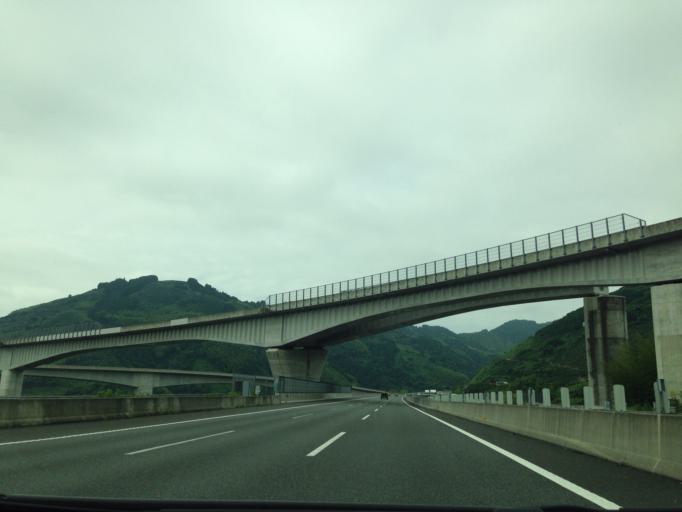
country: JP
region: Shizuoka
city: Shizuoka-shi
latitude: 35.0788
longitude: 138.4635
